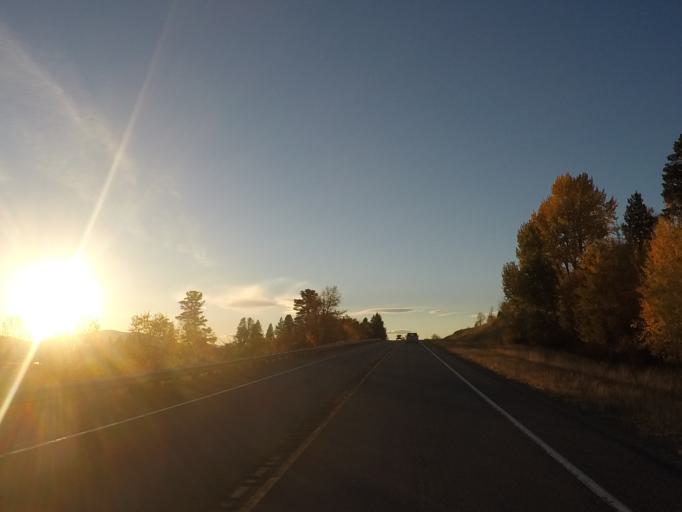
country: US
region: Montana
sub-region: Lewis and Clark County
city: Lincoln
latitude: 47.0184
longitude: -113.0897
